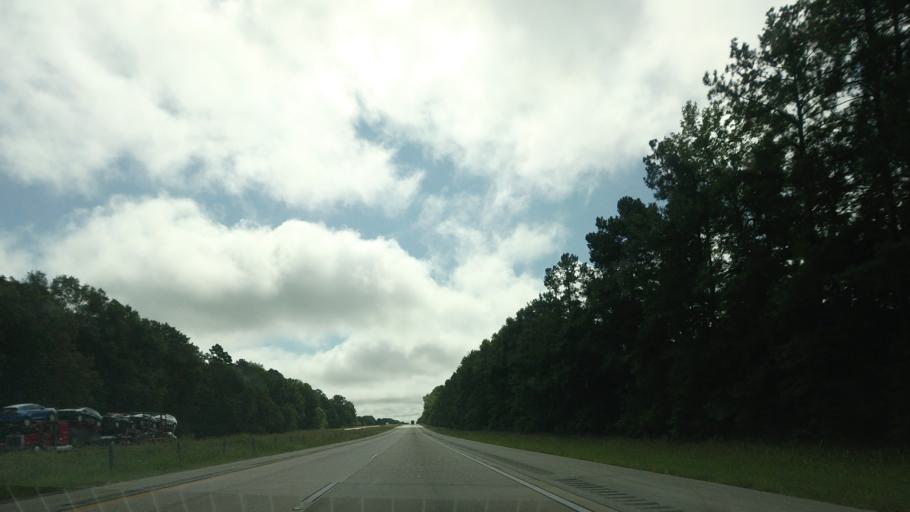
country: US
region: Georgia
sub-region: Twiggs County
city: Jeffersonville
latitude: 32.6093
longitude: -83.3364
